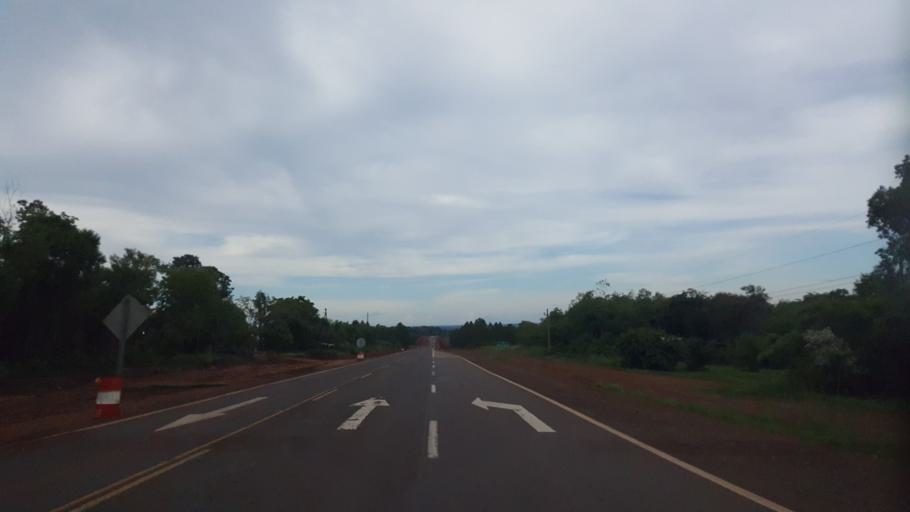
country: AR
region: Misiones
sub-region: Departamento de Candelaria
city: Loreto
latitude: -27.3491
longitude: -55.5477
